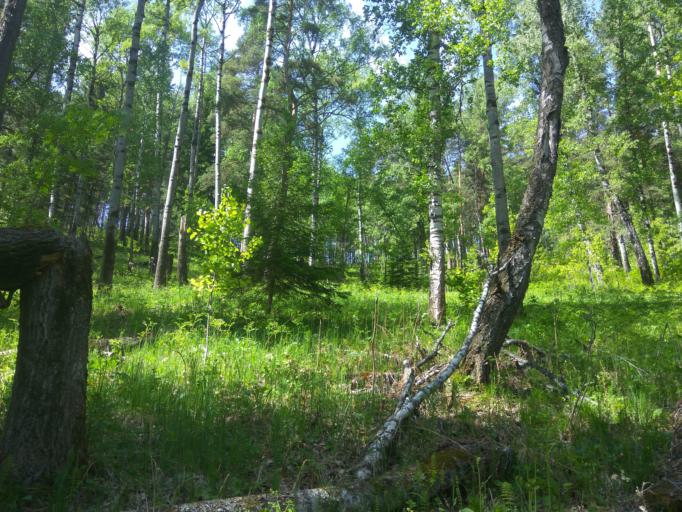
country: RU
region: Krasnoyarskiy
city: Krasnoyarsk
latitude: 55.9031
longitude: 92.9404
